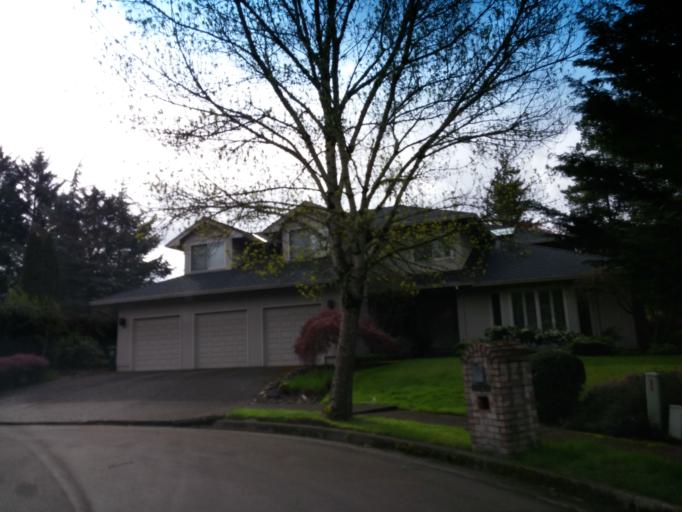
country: US
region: Oregon
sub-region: Washington County
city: Cedar Mill
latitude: 45.5383
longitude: -122.8127
